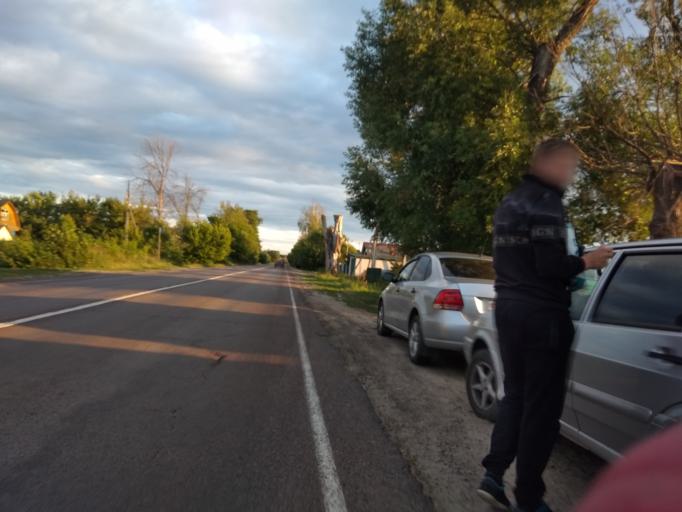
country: RU
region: Moskovskaya
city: Kerva
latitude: 55.5964
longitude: 39.7032
